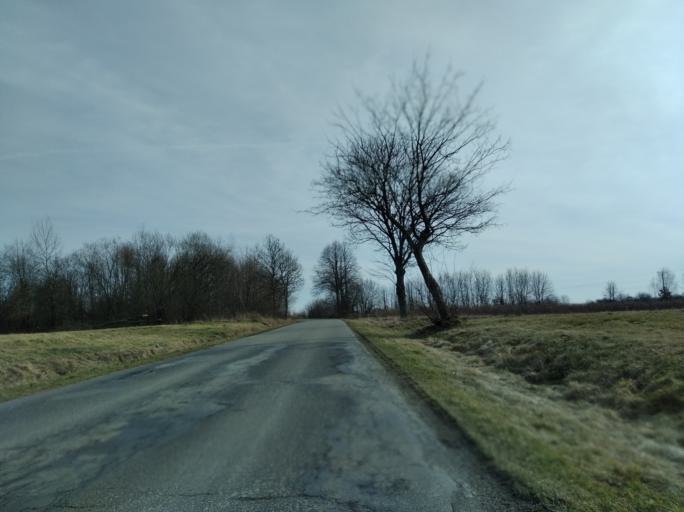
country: PL
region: Subcarpathian Voivodeship
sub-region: Powiat brzozowski
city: Stara Wies
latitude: 49.7133
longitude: 21.9860
